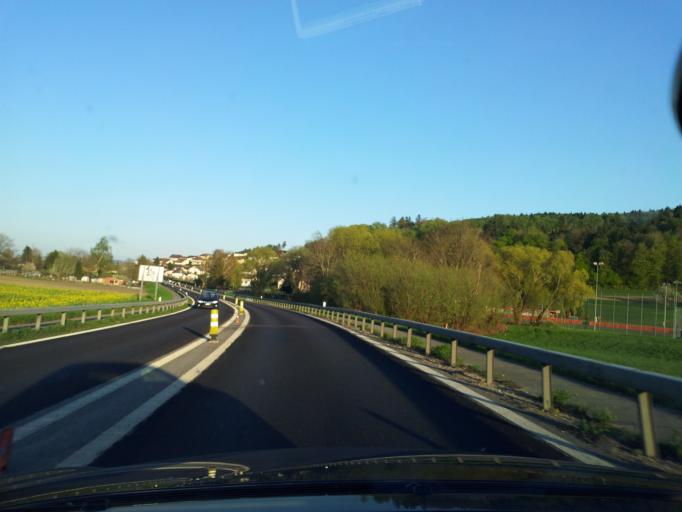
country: CH
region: Bern
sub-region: Biel/Bienne District
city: Brugg
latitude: 47.1184
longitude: 7.2801
